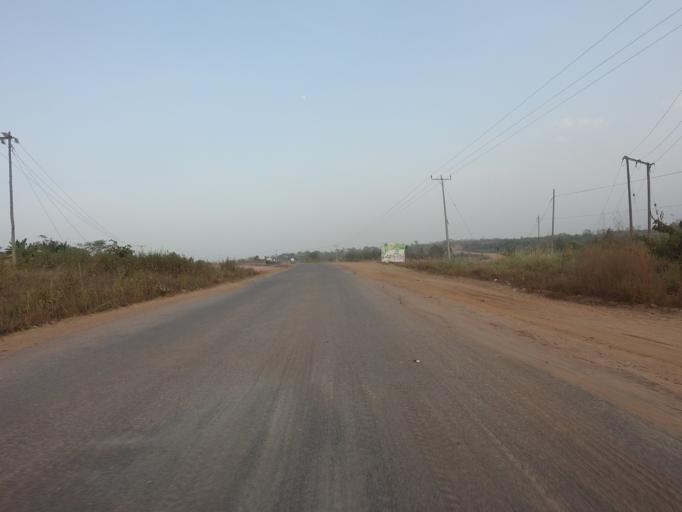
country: GH
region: Volta
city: Ho
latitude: 6.5756
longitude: 0.4196
